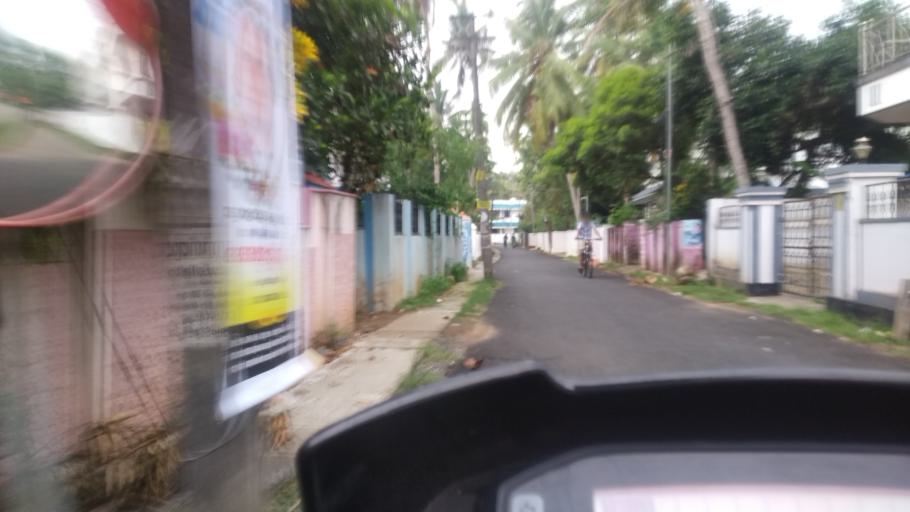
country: IN
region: Kerala
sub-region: Ernakulam
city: Elur
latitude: 10.0653
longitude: 76.2154
